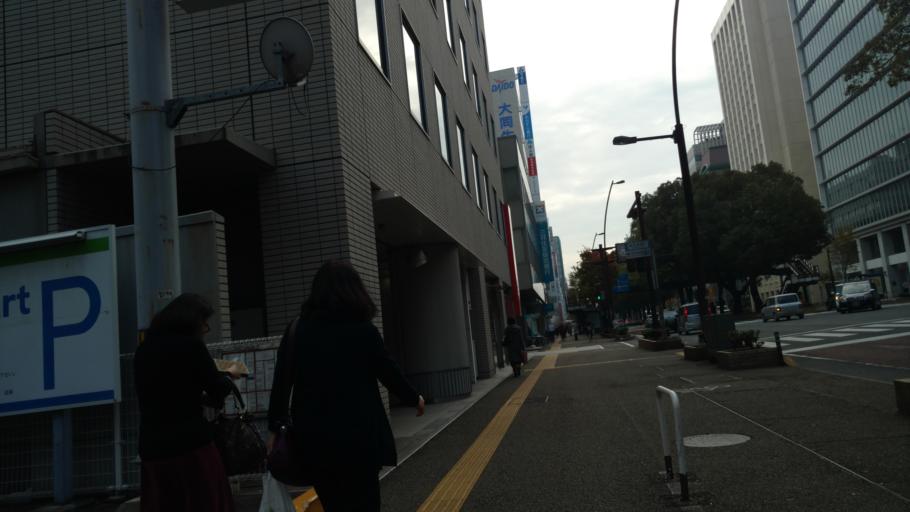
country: JP
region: Kagawa
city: Takamatsu-shi
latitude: 34.3449
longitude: 134.0484
